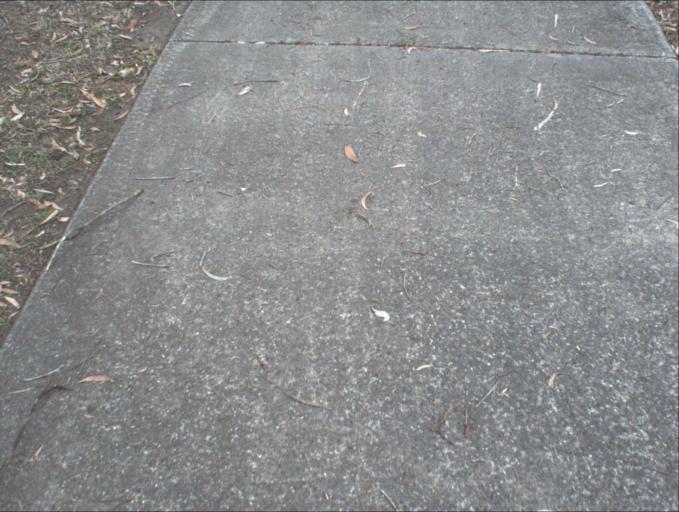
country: AU
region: Queensland
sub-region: Logan
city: Slacks Creek
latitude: -27.6498
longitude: 153.1403
